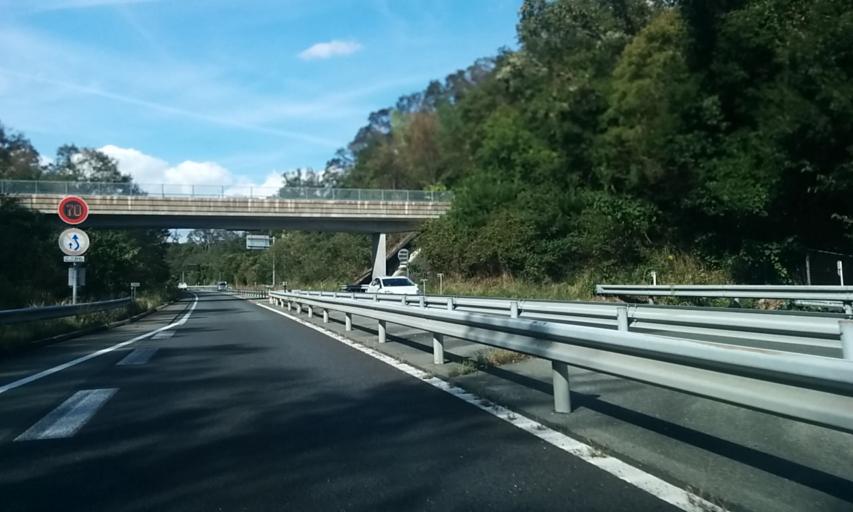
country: JP
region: Kyoto
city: Tanabe
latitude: 34.7790
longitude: 135.7733
